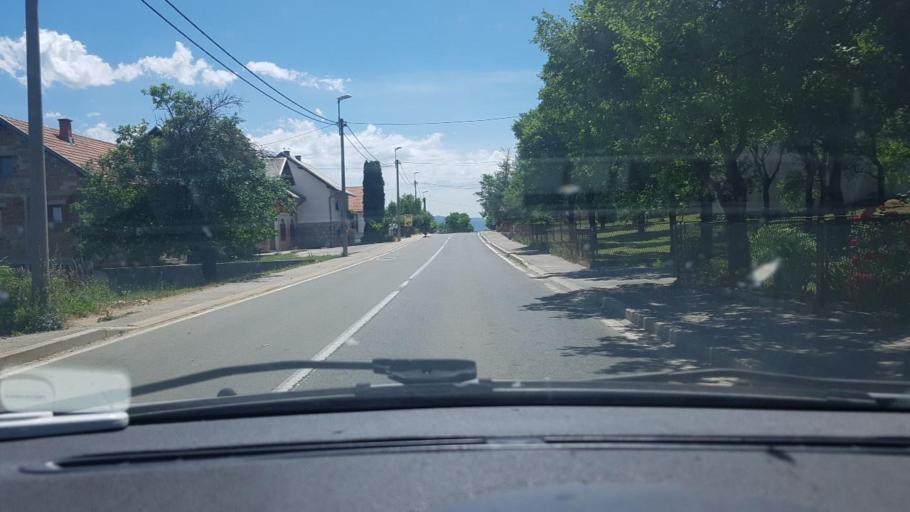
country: HR
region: Licko-Senjska
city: Otocac
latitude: 44.8623
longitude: 15.2623
